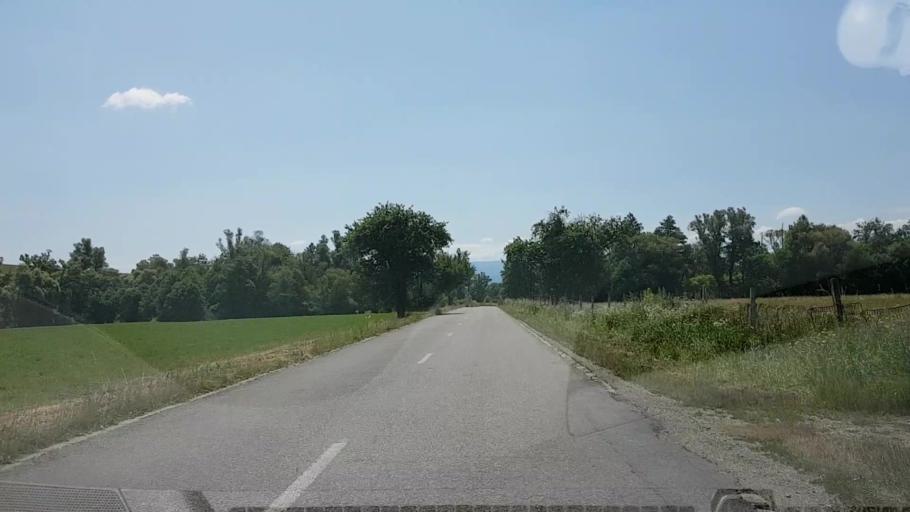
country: RO
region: Brasov
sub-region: Comuna Voila
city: Voila
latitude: 45.8597
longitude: 24.8269
